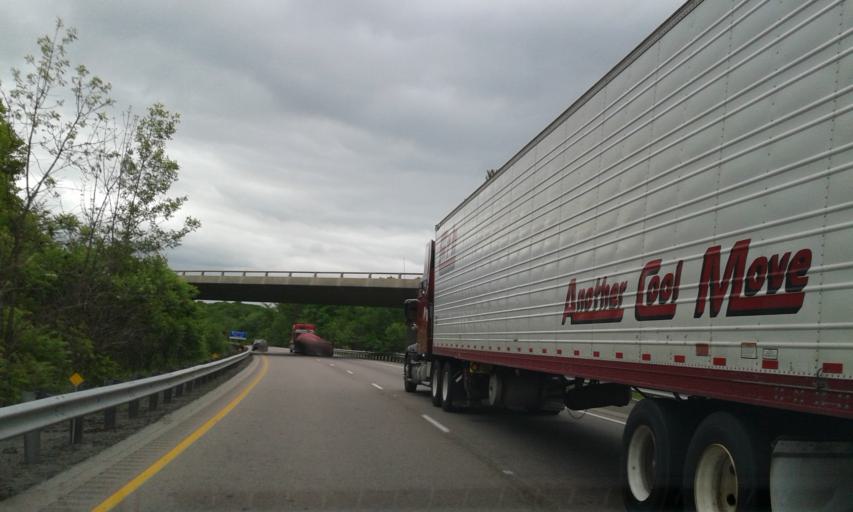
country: CA
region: Ontario
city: Brockville
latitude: 44.5187
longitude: -75.7883
